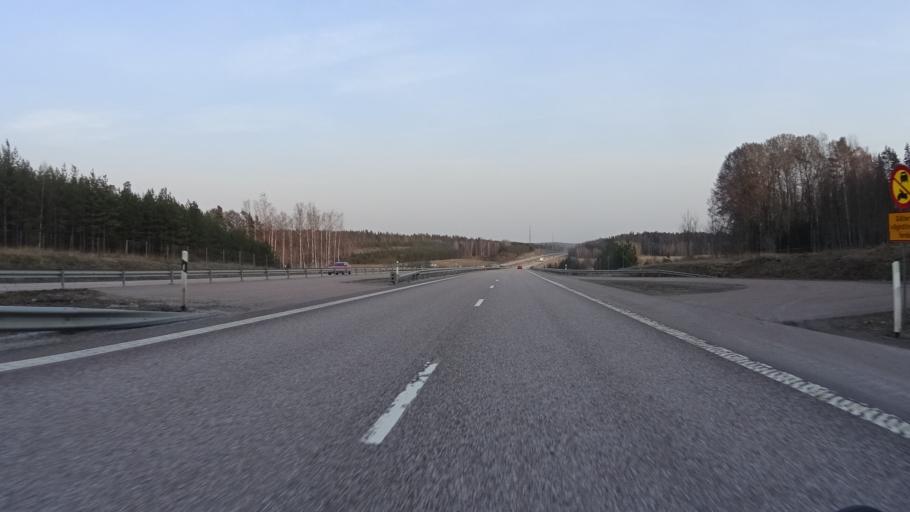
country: SE
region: Soedermanland
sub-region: Strangnas Kommun
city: Akers Styckebruk
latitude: 59.3010
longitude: 17.0854
